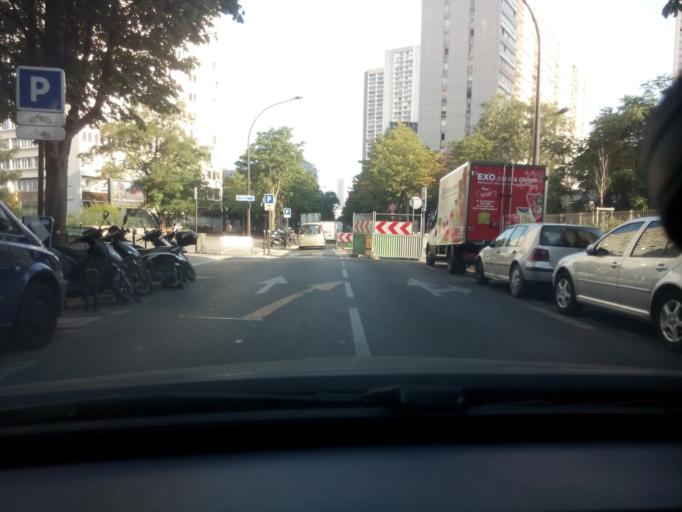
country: FR
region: Ile-de-France
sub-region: Departement du Val-de-Marne
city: Le Kremlin-Bicetre
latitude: 48.8224
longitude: 2.3677
